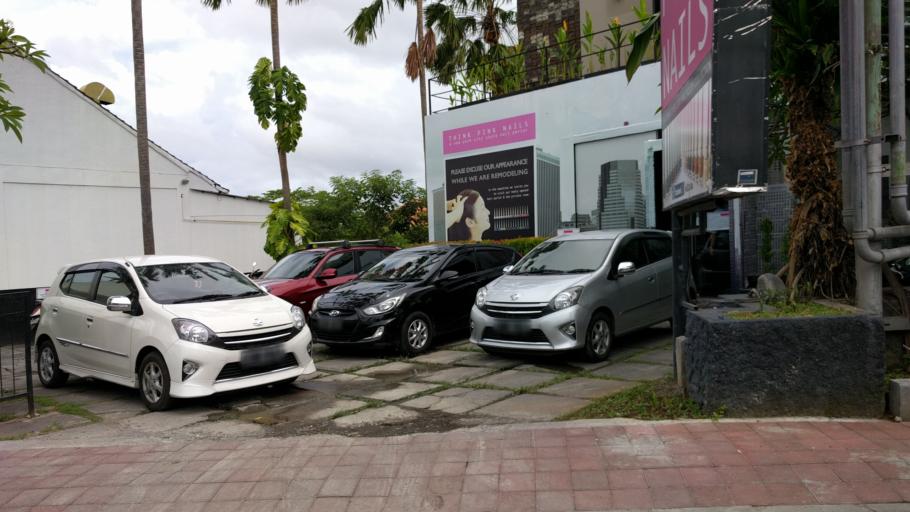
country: ID
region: Bali
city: Kuta
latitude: -8.6725
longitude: 115.1558
